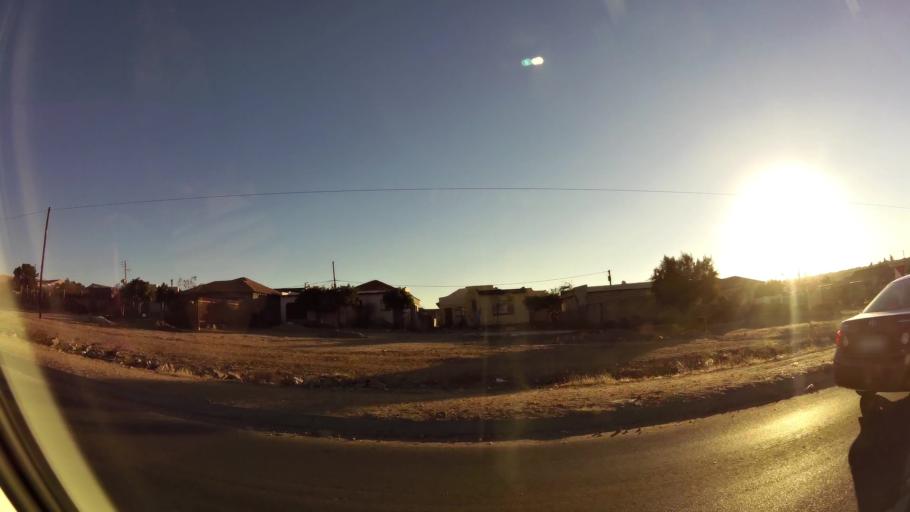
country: ZA
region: Limpopo
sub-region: Capricorn District Municipality
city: Polokwane
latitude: -23.8443
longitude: 29.3533
